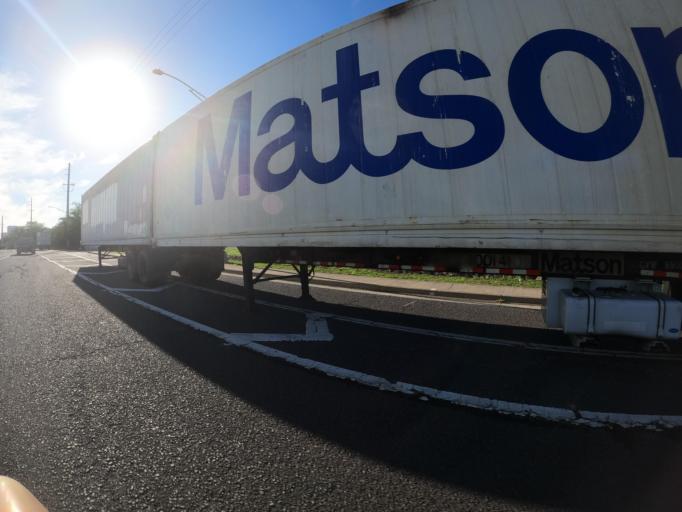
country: US
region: Hawaii
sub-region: Honolulu County
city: Honolulu
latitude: 21.3073
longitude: -157.8809
